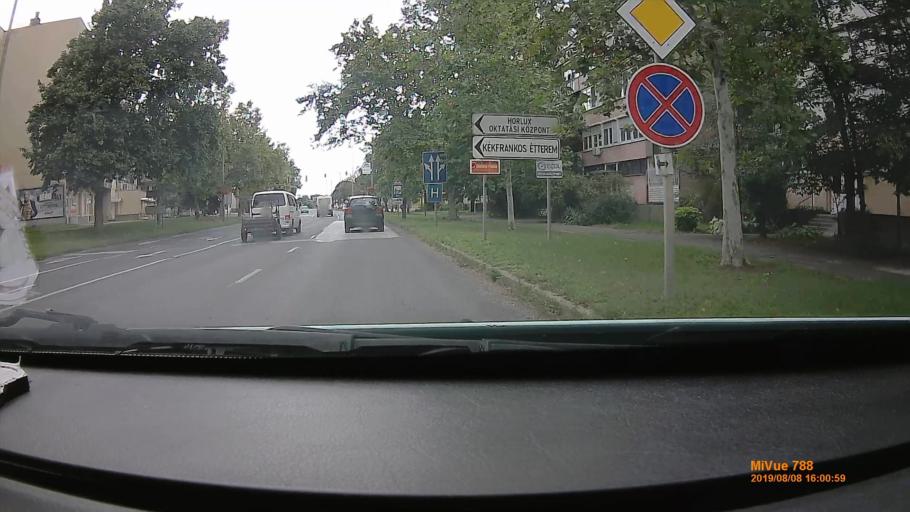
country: HU
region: Szabolcs-Szatmar-Bereg
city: Mateszalka
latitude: 47.9540
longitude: 22.3253
